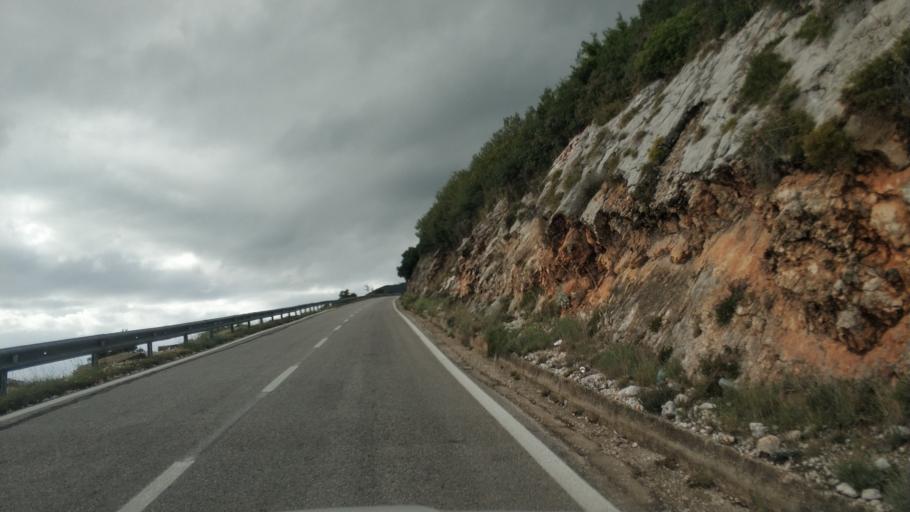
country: AL
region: Vlore
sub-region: Rrethi i Vlores
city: Vranisht
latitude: 40.1779
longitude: 19.6012
